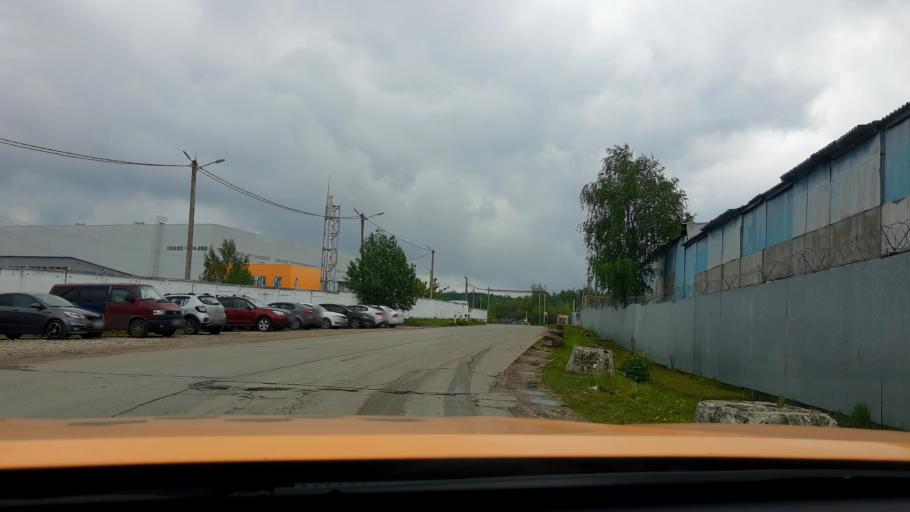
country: RU
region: Moskovskaya
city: L'vovskiy
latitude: 55.3277
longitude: 37.4976
